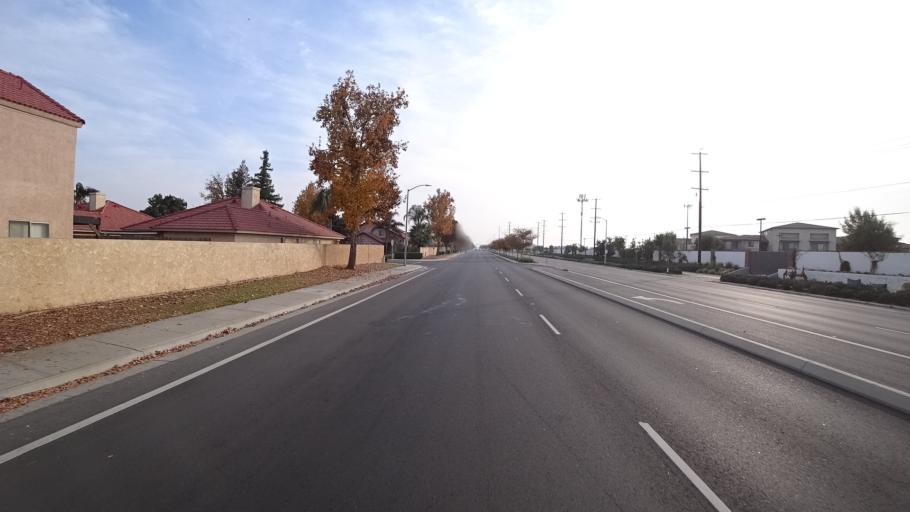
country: US
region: California
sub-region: Kern County
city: Greenacres
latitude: 35.3218
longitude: -119.1279
